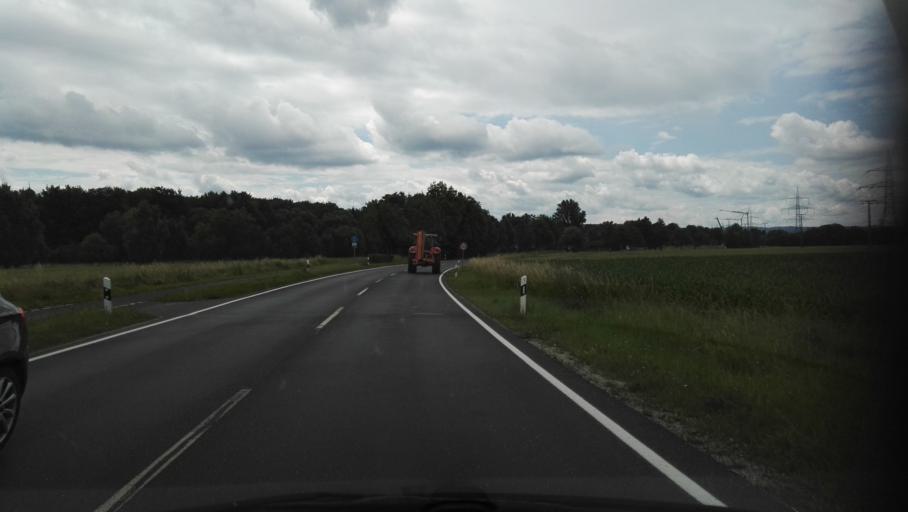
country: DE
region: Bavaria
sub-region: Upper Franconia
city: Redwitz an der Rodach
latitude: 50.1789
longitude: 11.2026
